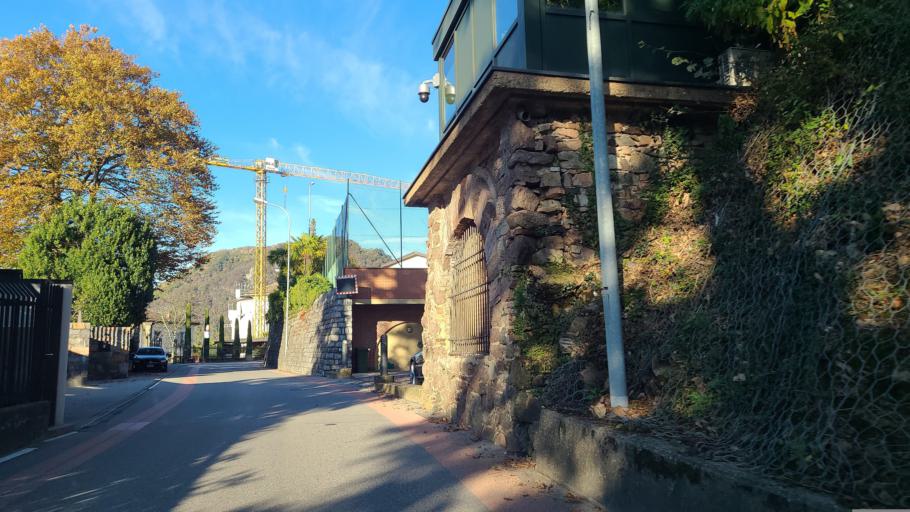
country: IT
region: Lombardy
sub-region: Provincia di Varese
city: Brusimpiano
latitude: 45.9466
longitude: 8.9041
